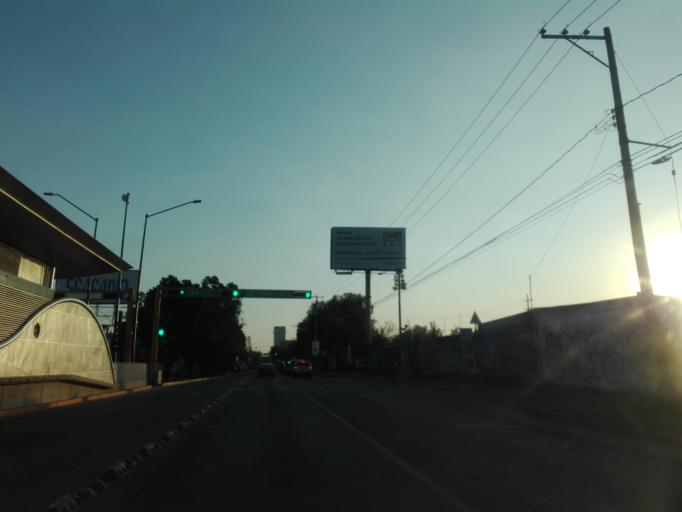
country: MX
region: Guanajuato
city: Leon
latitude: 21.1212
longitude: -101.6501
